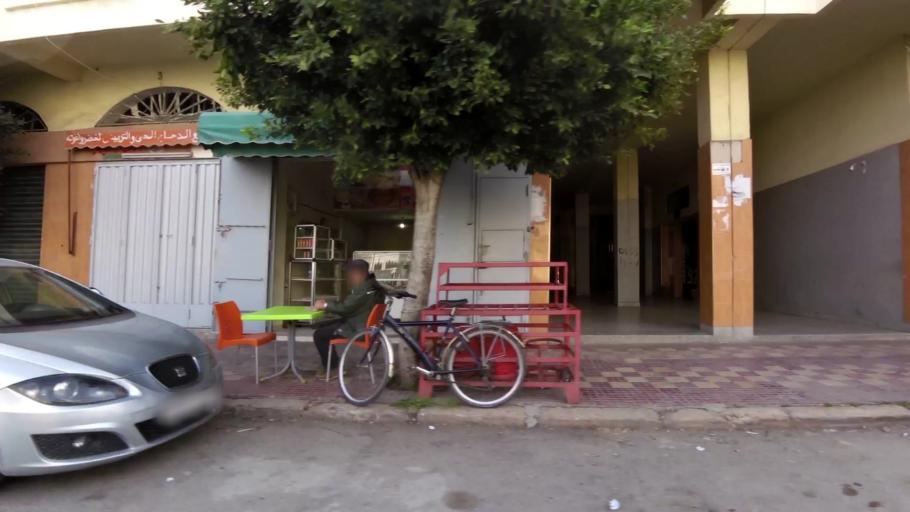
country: MA
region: Tanger-Tetouan
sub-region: Tanger-Assilah
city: Tangier
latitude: 35.7410
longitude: -5.7980
